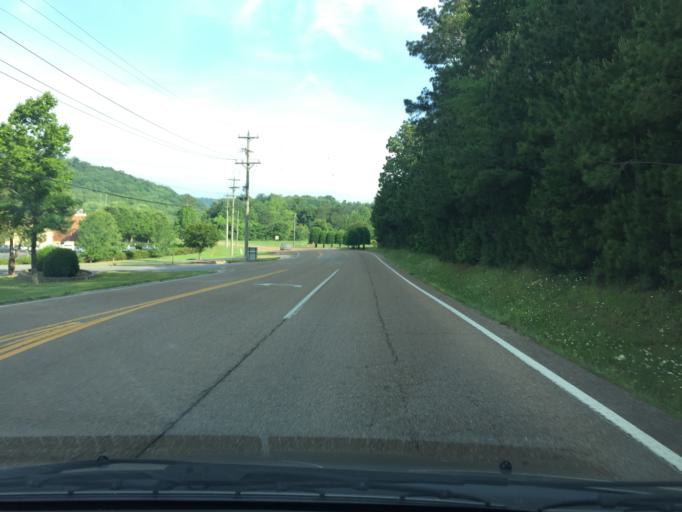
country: US
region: Tennessee
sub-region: Hamilton County
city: Apison
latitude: 35.0415
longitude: -85.0300
